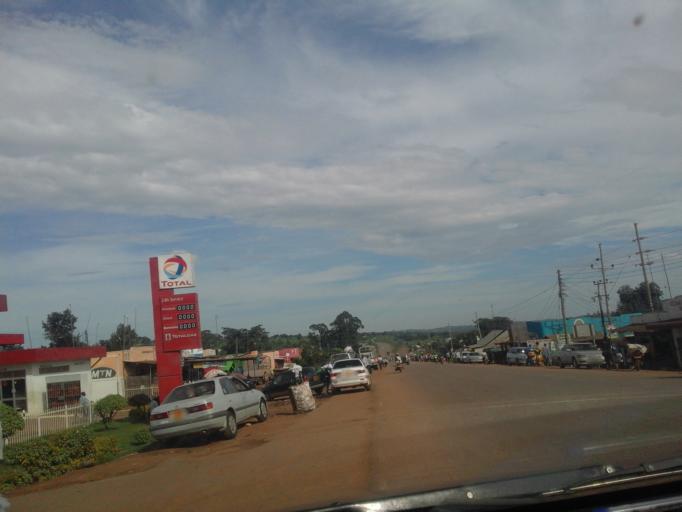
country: UG
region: Central Region
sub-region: Lwengo District
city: Lwengo
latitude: -0.3531
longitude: 31.5534
